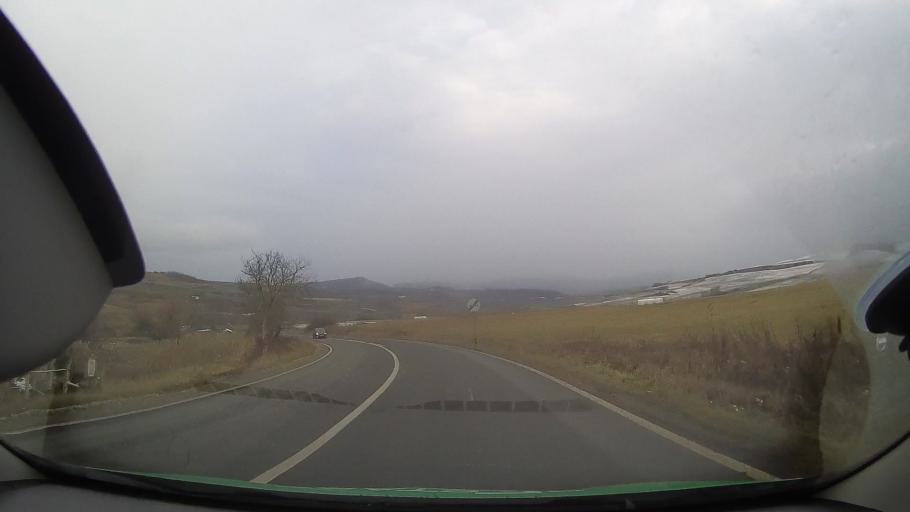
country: RO
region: Sibiu
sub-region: Comuna Blajel
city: Blajel
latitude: 46.2376
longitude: 24.3043
